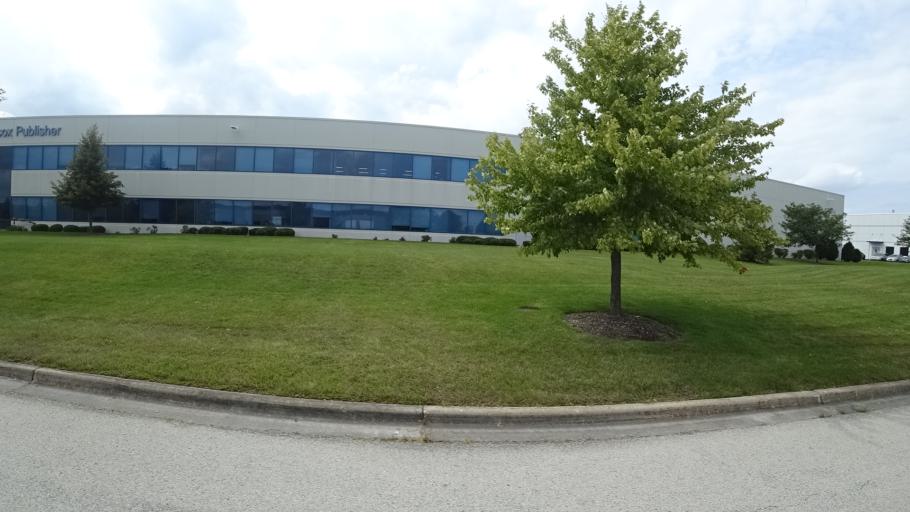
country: US
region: Illinois
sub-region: Cook County
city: Tinley Park
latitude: 41.5538
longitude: -87.8007
